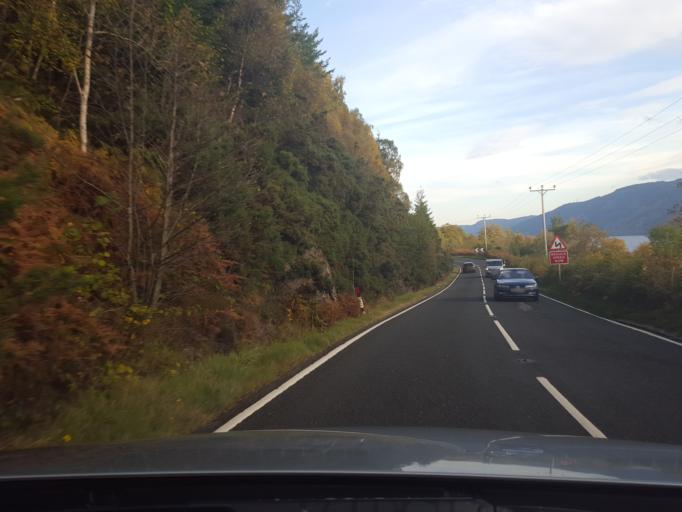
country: GB
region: Scotland
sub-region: Highland
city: Beauly
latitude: 57.2194
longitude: -4.5824
